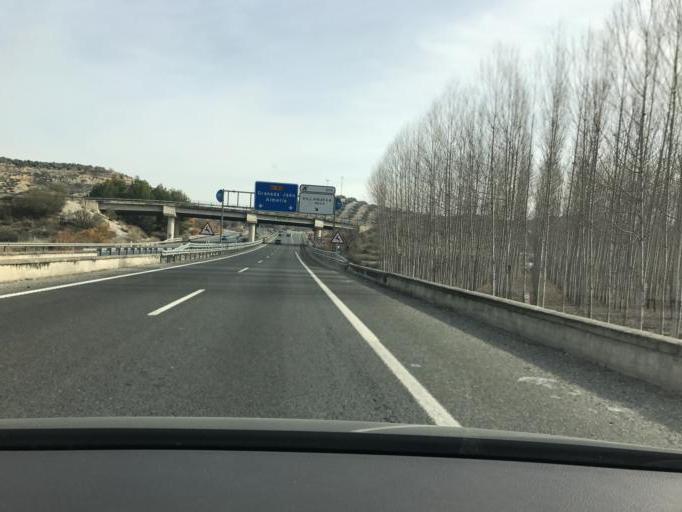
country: ES
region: Andalusia
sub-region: Provincia de Granada
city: Villanueva de Mesia
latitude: 37.1930
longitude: -4.0026
